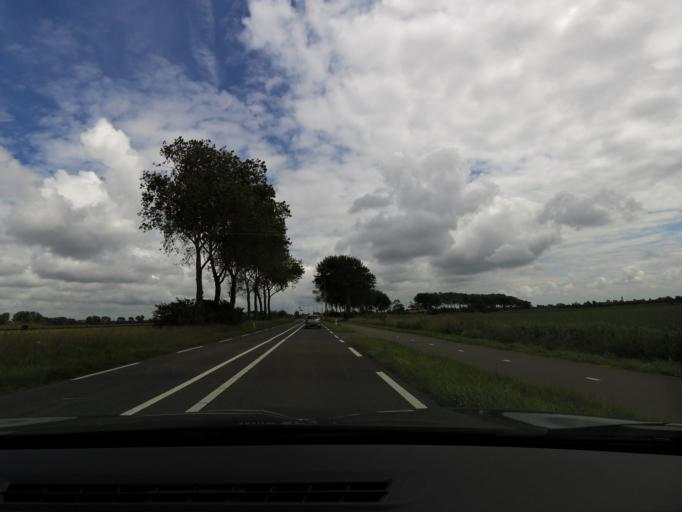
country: NL
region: Zeeland
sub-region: Gemeente Vlissingen
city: Vlissingen
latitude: 51.4869
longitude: 3.5360
